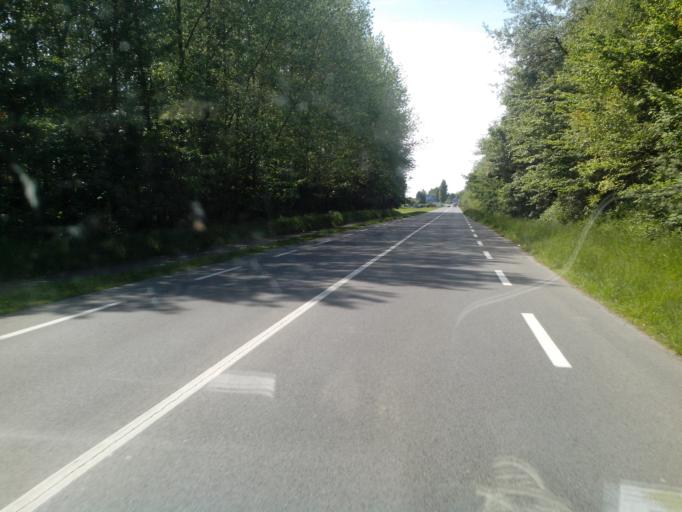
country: FR
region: Nord-Pas-de-Calais
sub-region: Departement du Pas-de-Calais
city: Etaples
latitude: 50.5076
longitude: 1.6618
